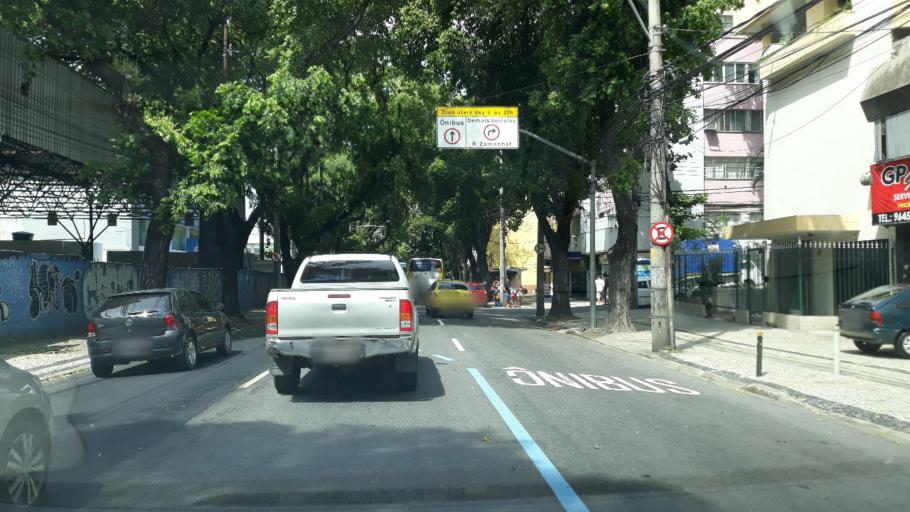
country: BR
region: Rio de Janeiro
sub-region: Rio De Janeiro
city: Rio de Janeiro
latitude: -22.9158
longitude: -43.2086
